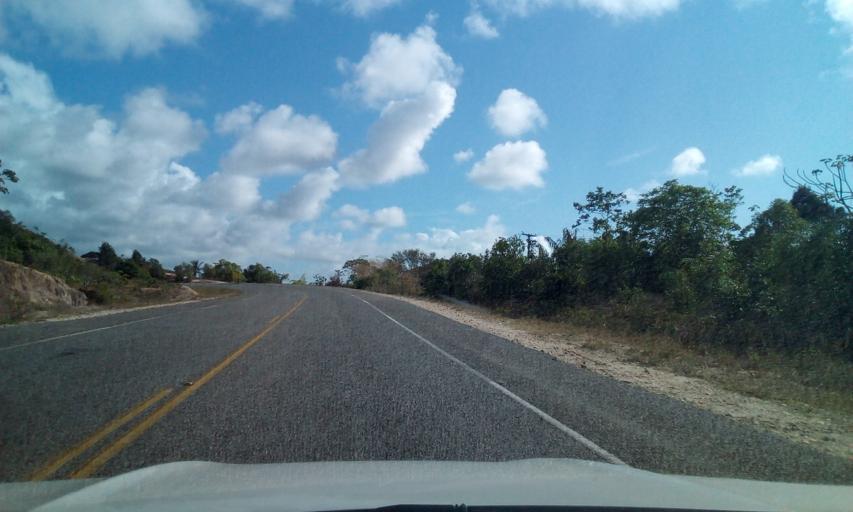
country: BR
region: Bahia
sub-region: Conde
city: Conde
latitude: -11.7181
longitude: -37.5730
